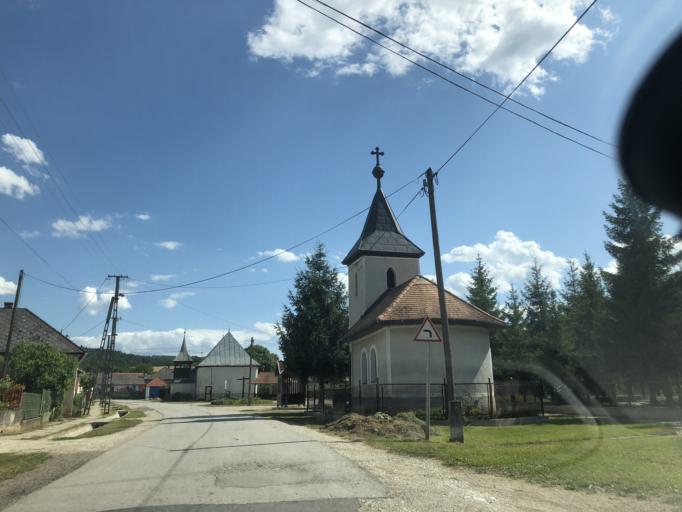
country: HU
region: Borsod-Abauj-Zemplen
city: Szendro
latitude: 48.5428
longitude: 20.8034
